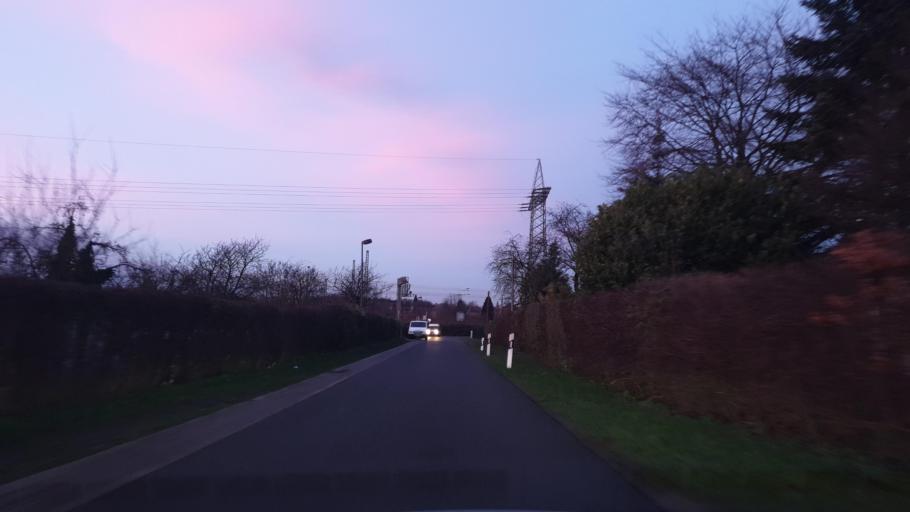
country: DE
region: Lower Saxony
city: Osnabrueck
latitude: 52.2597
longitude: 8.0346
